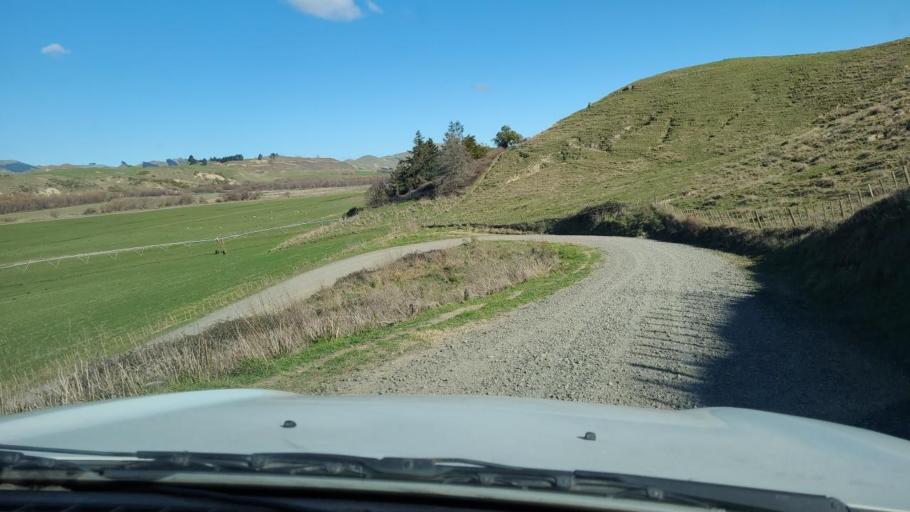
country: NZ
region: Hawke's Bay
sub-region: Hastings District
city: Hastings
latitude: -39.7632
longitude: 176.8109
